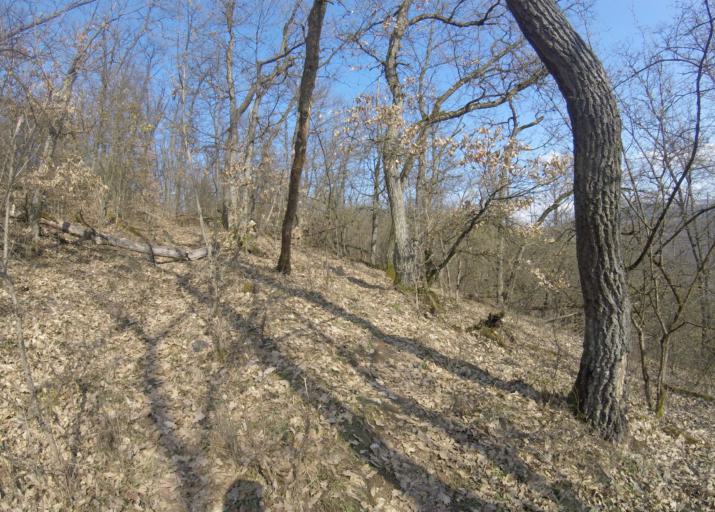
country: HU
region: Heves
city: Belapatfalva
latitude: 47.9896
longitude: 20.3386
